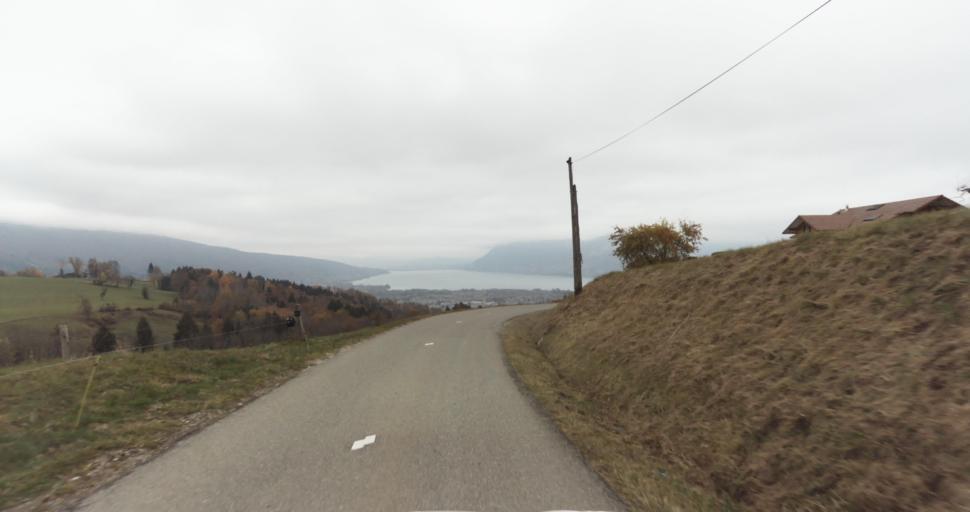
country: FR
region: Rhone-Alpes
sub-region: Departement de la Haute-Savoie
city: Saint-Jorioz
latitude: 45.8091
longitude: 6.1652
